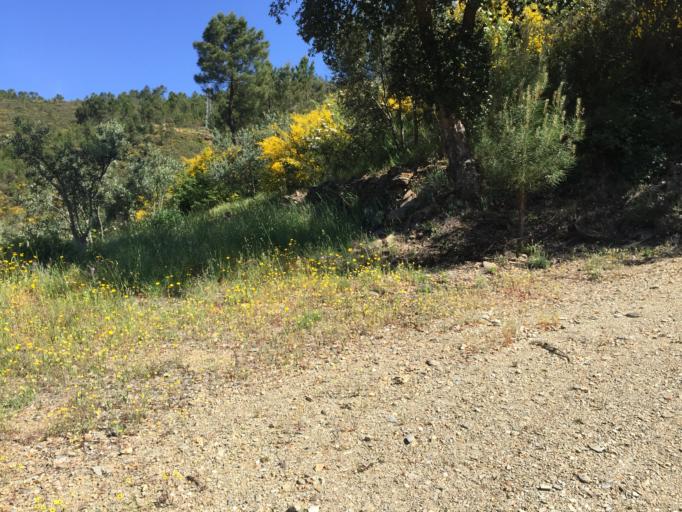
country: PT
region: Coimbra
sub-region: Pampilhosa da Serra
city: Pampilhosa da Serra
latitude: 40.0892
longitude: -7.7814
